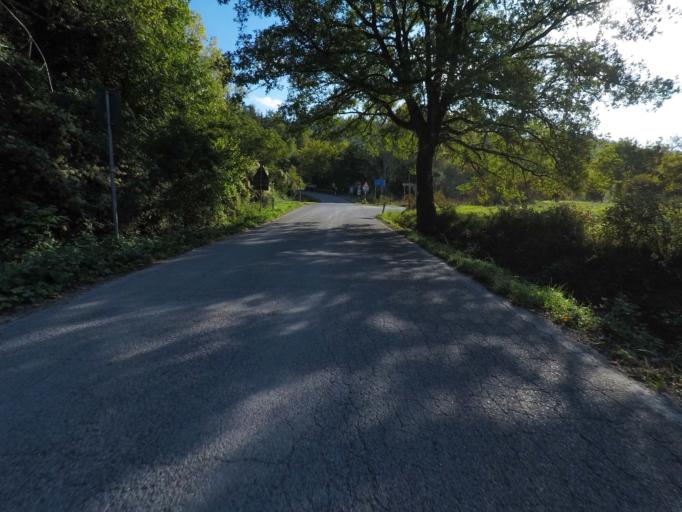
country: IT
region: Tuscany
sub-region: Provincia di Siena
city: Radda in Chianti
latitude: 43.4682
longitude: 11.3733
